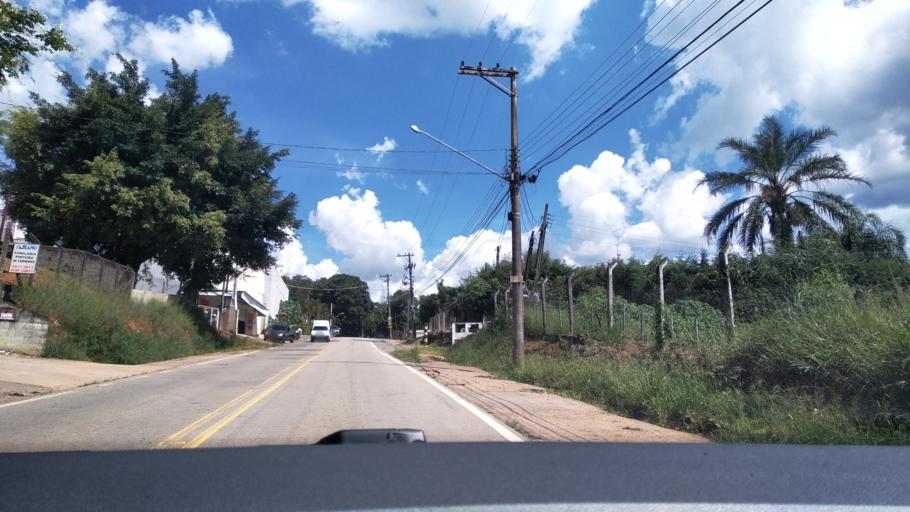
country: BR
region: Sao Paulo
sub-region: Varzea Paulista
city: Varzea Paulista
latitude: -23.2445
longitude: -46.8750
